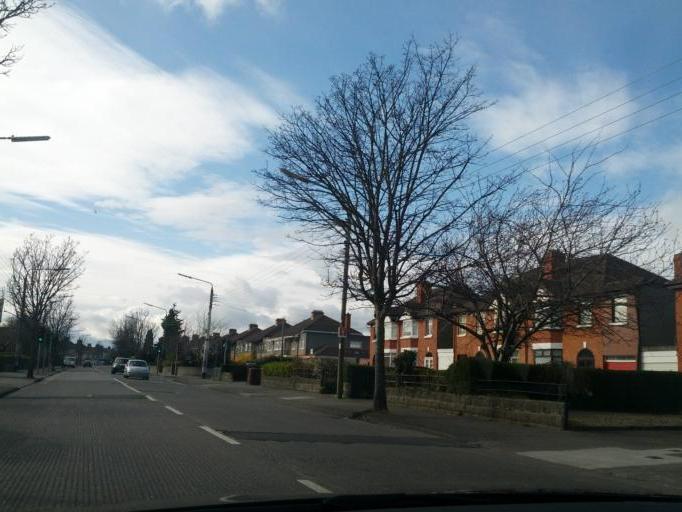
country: IE
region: Leinster
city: Marino
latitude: 53.3782
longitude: -6.2292
